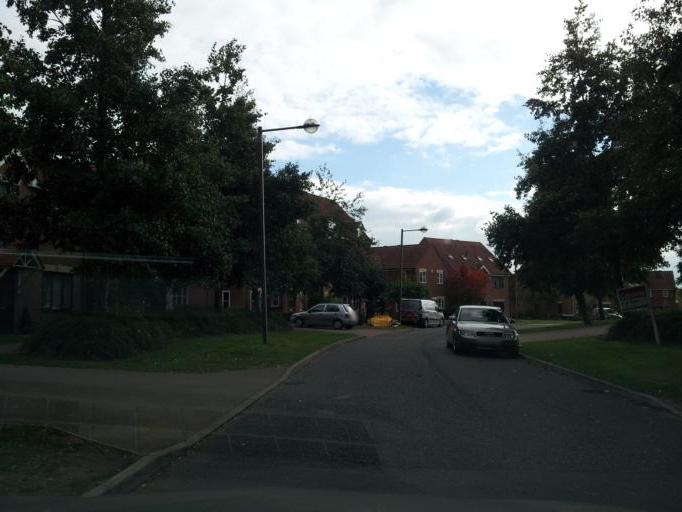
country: GB
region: England
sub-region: Milton Keynes
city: Shenley Church End
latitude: 52.0030
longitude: -0.7964
